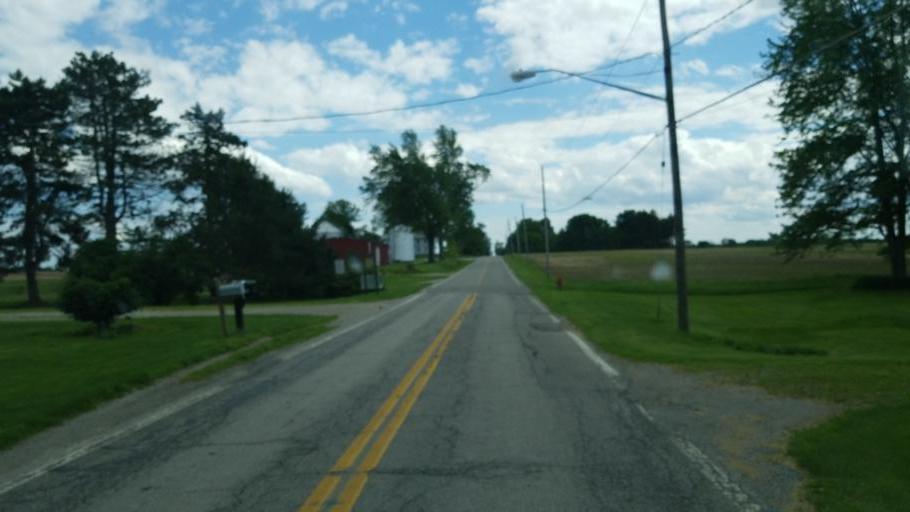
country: US
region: Ohio
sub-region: Huron County
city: Plymouth
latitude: 41.0981
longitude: -82.6114
